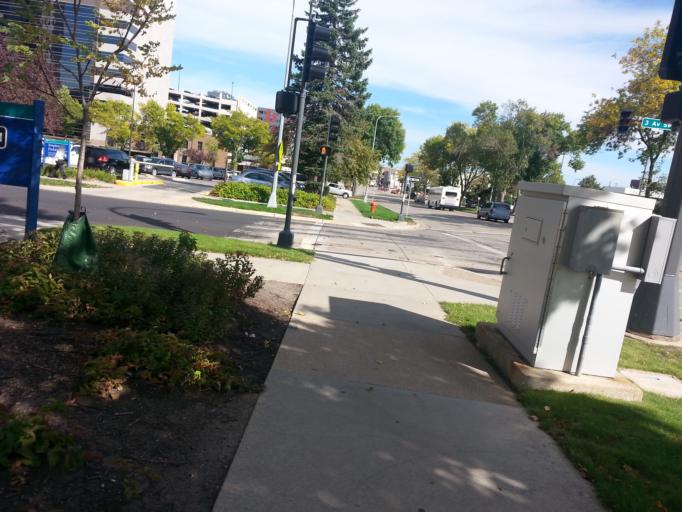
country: US
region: Minnesota
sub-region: Olmsted County
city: Rochester
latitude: 44.0194
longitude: -92.4676
